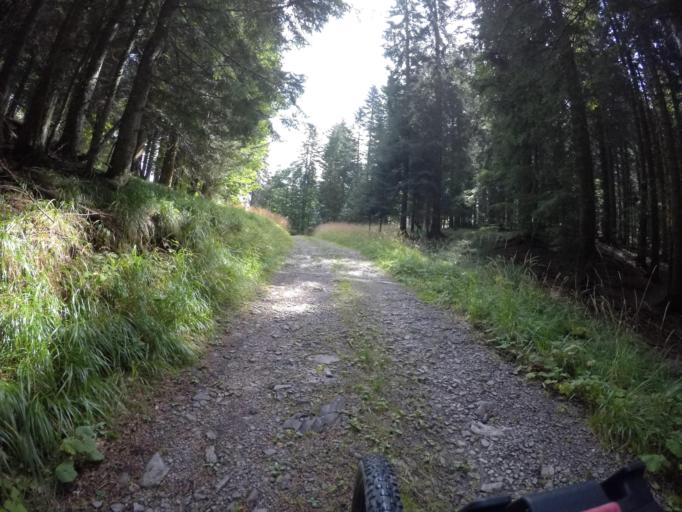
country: IT
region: Friuli Venezia Giulia
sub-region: Provincia di Udine
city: Paularo
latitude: 46.5108
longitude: 13.2037
